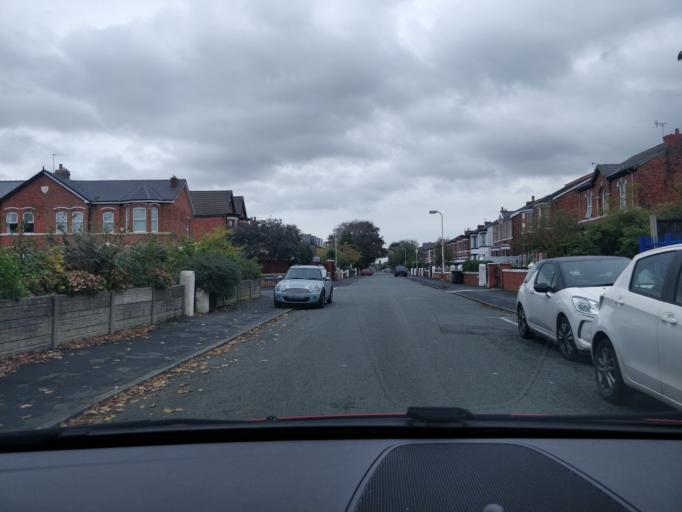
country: GB
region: England
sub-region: Sefton
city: Southport
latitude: 53.6411
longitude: -2.9940
